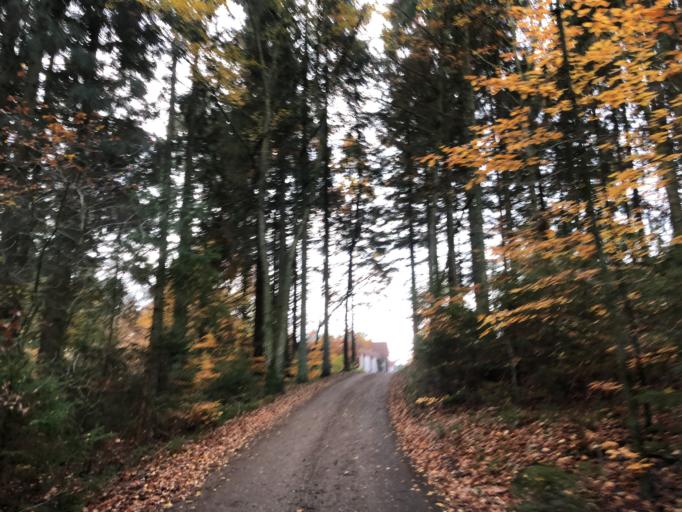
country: DK
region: Central Jutland
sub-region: Silkeborg Kommune
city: Silkeborg
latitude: 56.1421
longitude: 9.4814
